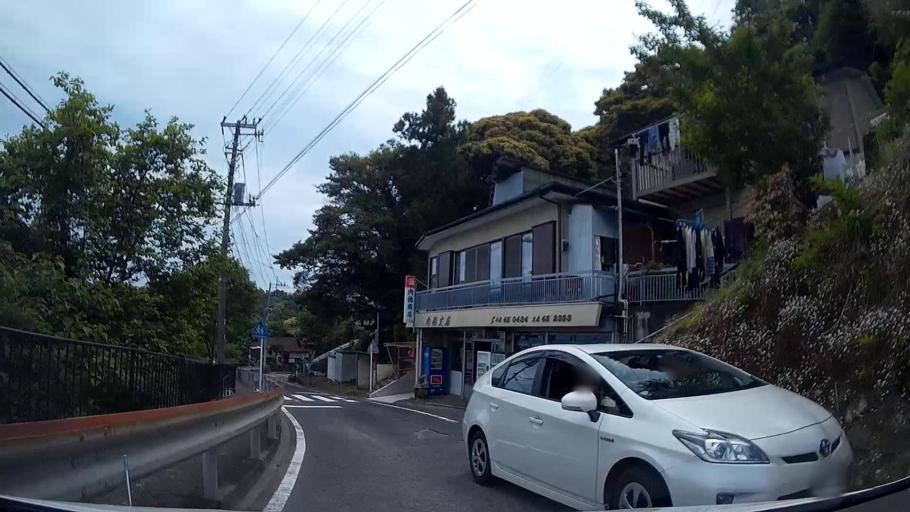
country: JP
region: Shizuoka
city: Ito
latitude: 34.9503
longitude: 139.1316
